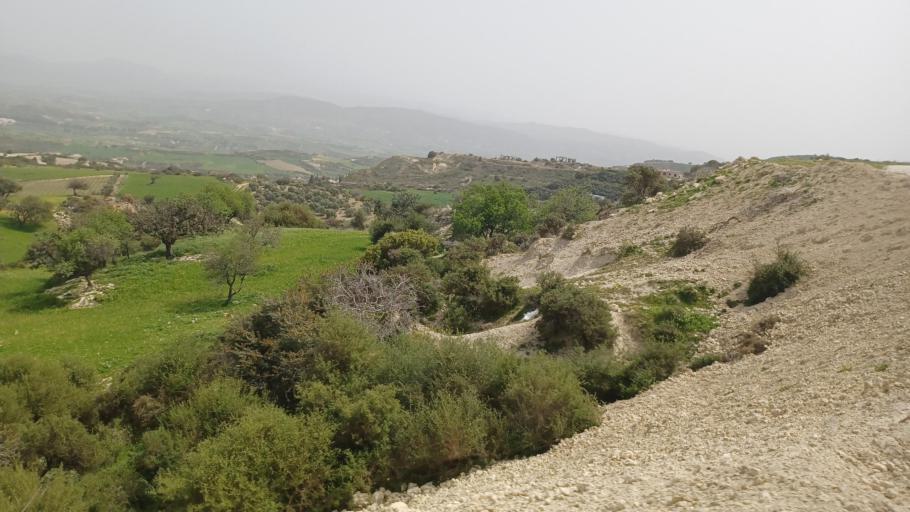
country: CY
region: Pafos
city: Polis
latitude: 35.0042
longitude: 32.3991
